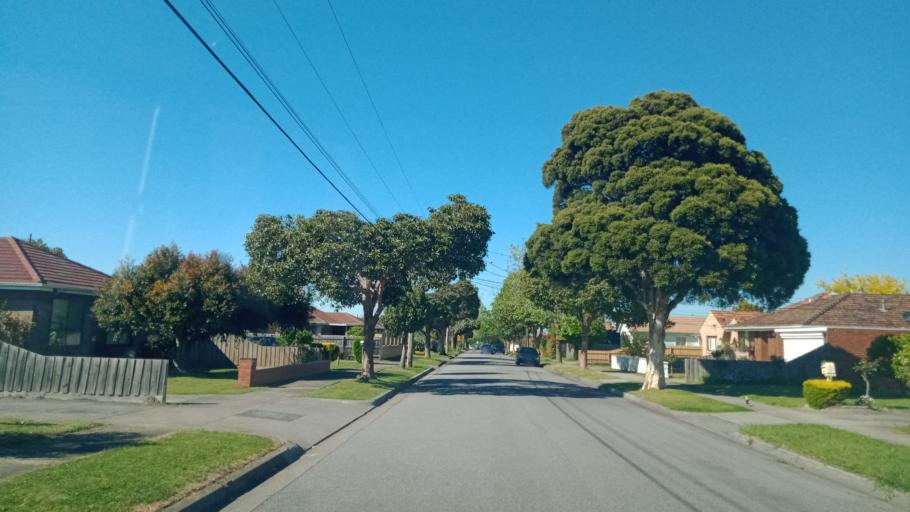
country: AU
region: Victoria
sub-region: Greater Dandenong
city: Springvale
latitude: -37.9357
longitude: 145.1655
